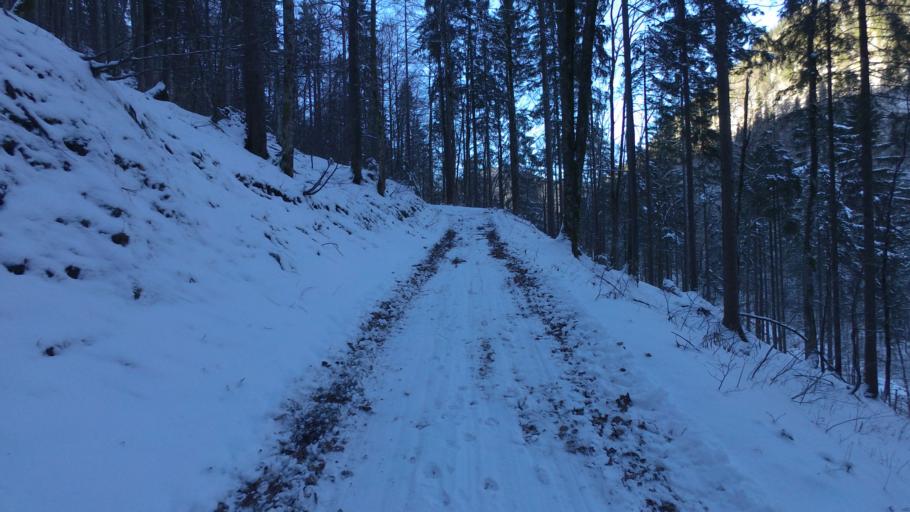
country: DE
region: Bavaria
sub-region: Upper Bavaria
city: Bergen
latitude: 47.7210
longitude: 12.5724
